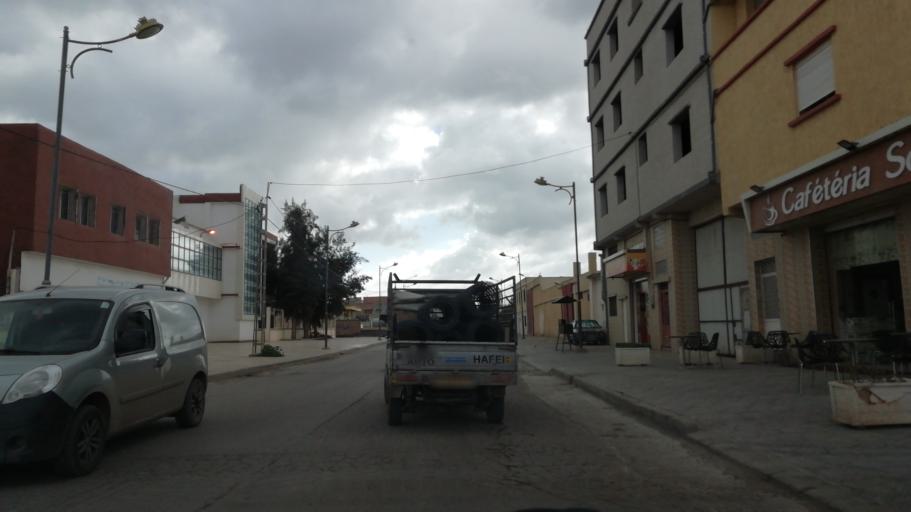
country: DZ
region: Oran
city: Sidi ech Chahmi
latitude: 35.6572
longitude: -0.5285
